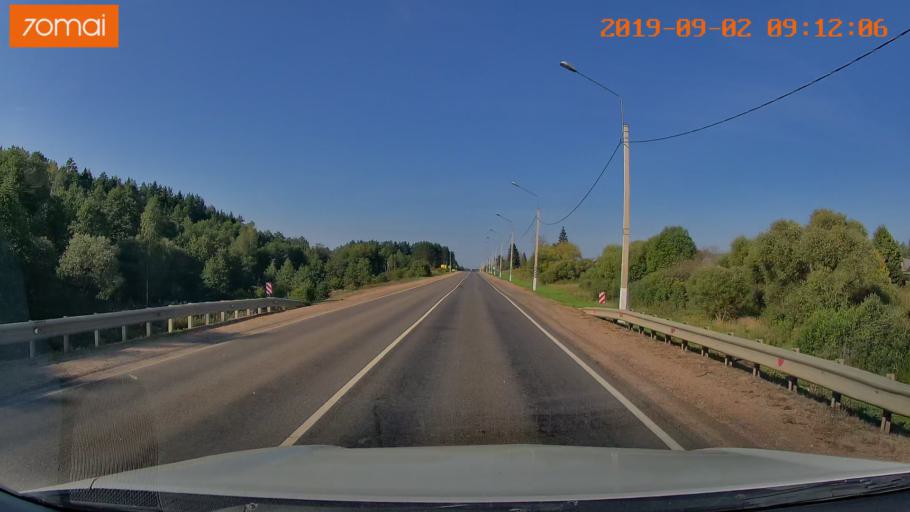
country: RU
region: Kaluga
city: Myatlevo
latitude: 54.8630
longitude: 35.5628
